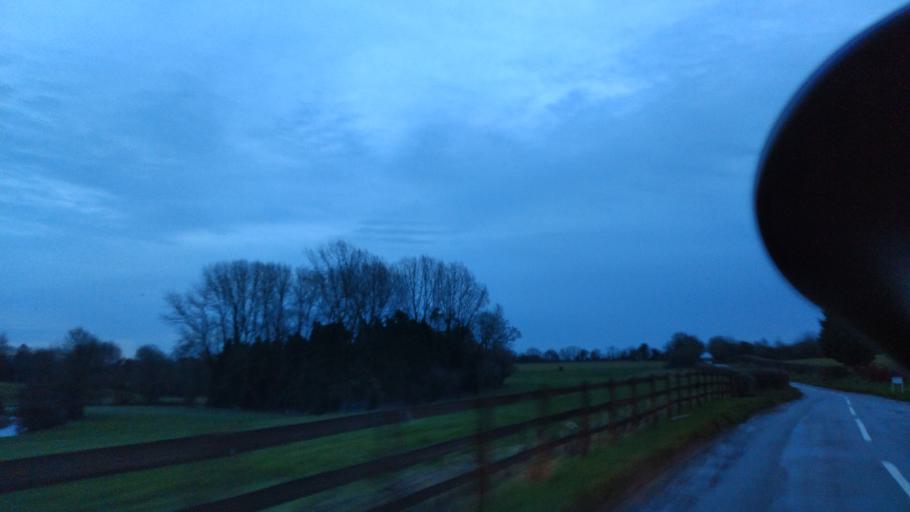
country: GB
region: England
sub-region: Oxfordshire
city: Shrivenham
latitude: 51.6125
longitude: -1.6793
